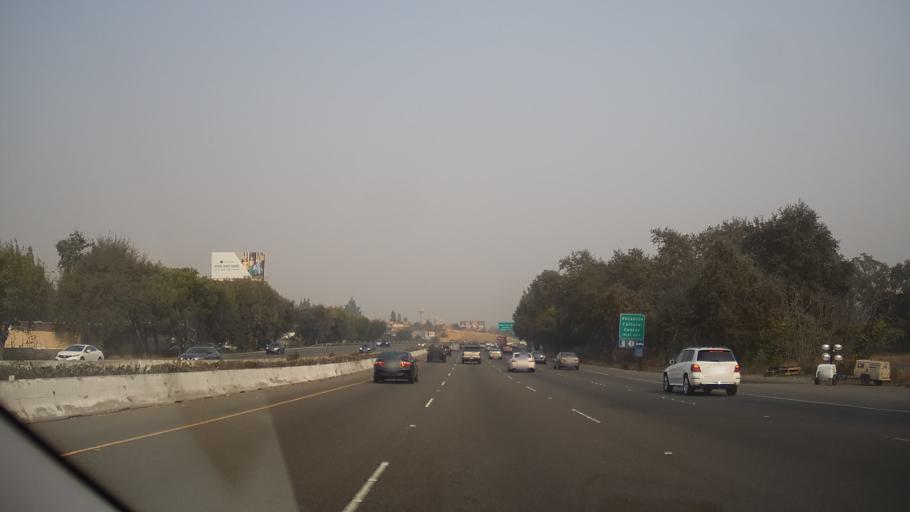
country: US
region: California
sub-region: Solano County
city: Vacaville
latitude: 38.3570
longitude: -121.9756
